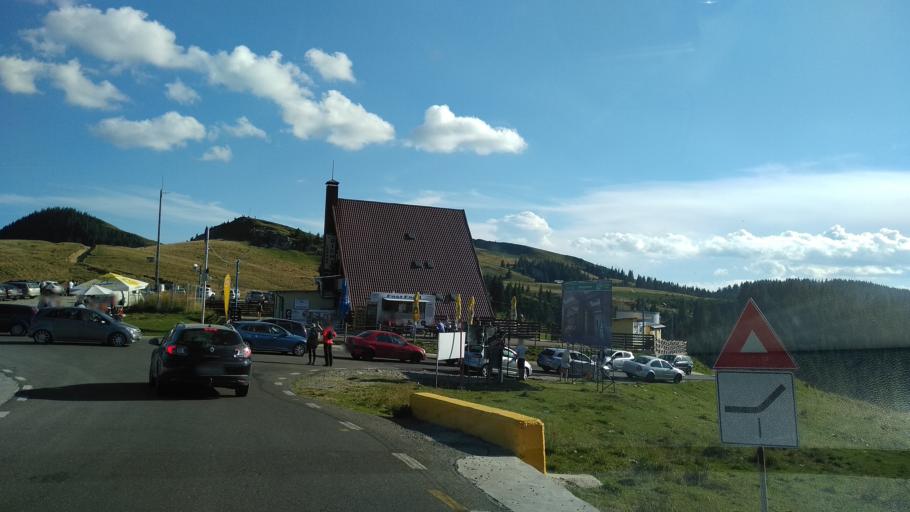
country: RO
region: Dambovita
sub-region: Comuna Moroeni
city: Glod
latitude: 45.3275
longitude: 25.4633
